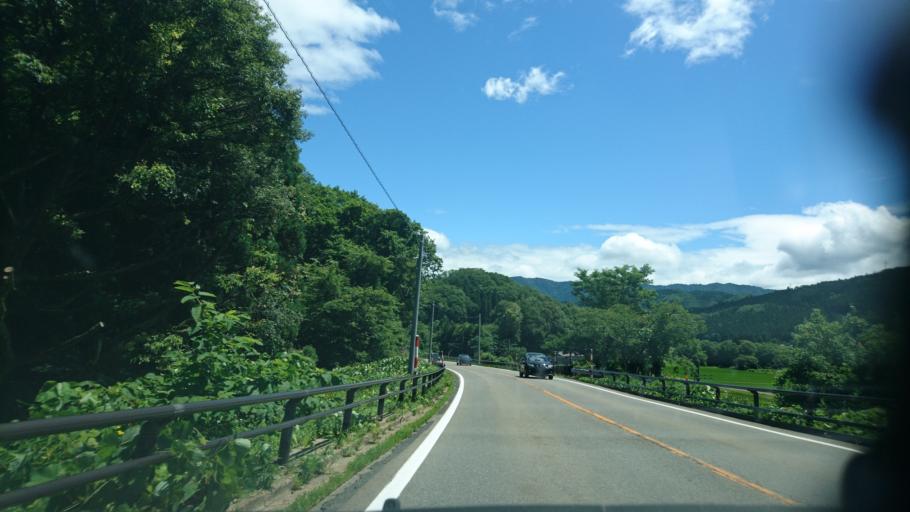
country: JP
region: Akita
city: Kakunodatemachi
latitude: 39.6659
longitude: 140.6881
